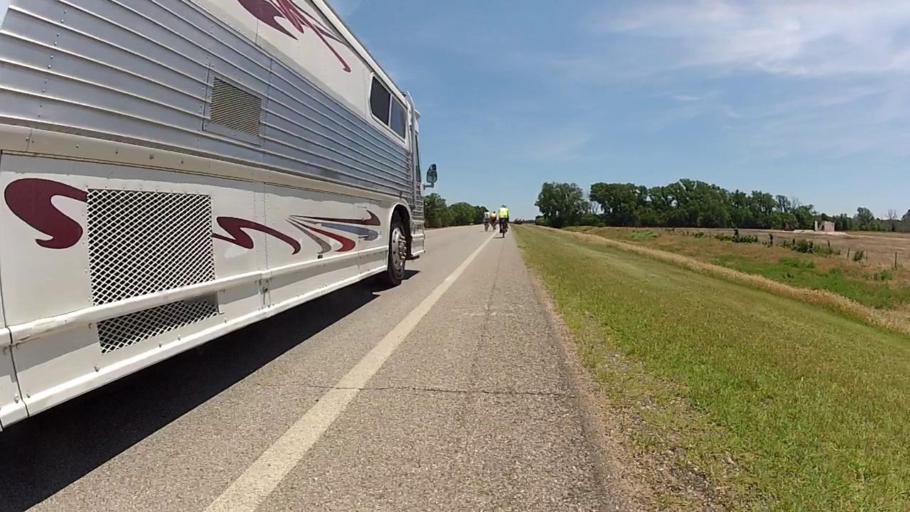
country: US
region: Kansas
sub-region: Barber County
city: Medicine Lodge
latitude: 37.2534
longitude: -98.4559
